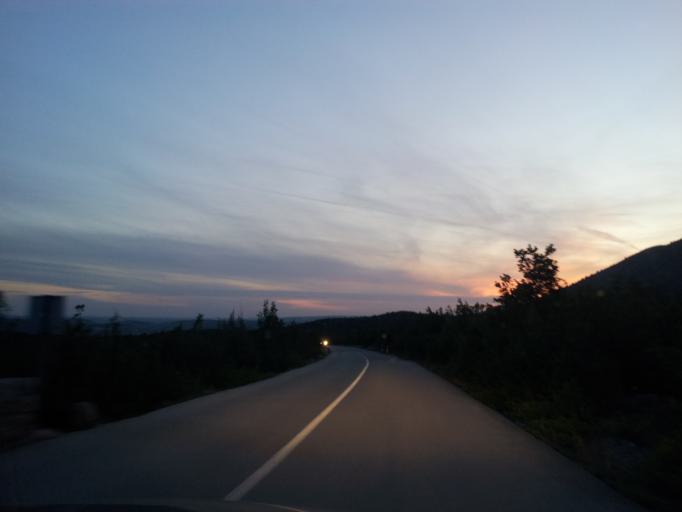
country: HR
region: Zadarska
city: Obrovac
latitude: 44.2318
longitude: 15.6762
